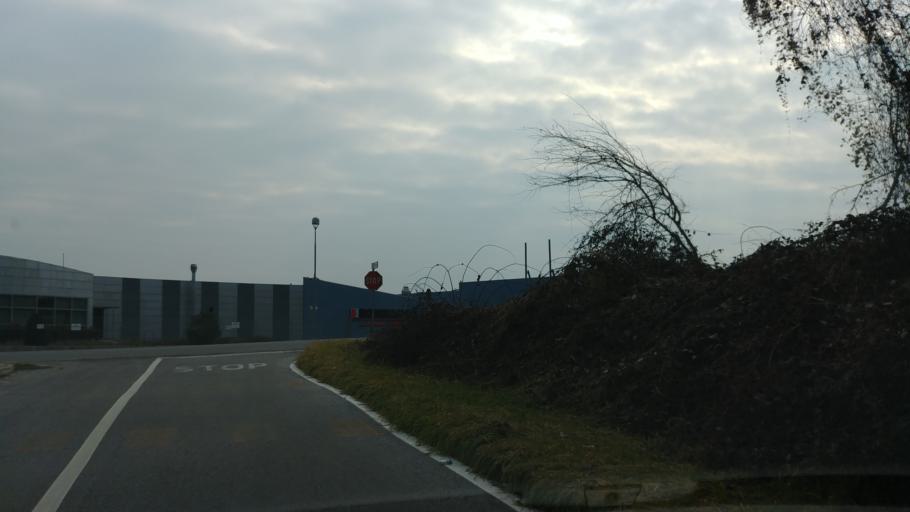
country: IT
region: Piedmont
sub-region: Provincia di Cuneo
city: Fossano
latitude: 44.5438
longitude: 7.7250
